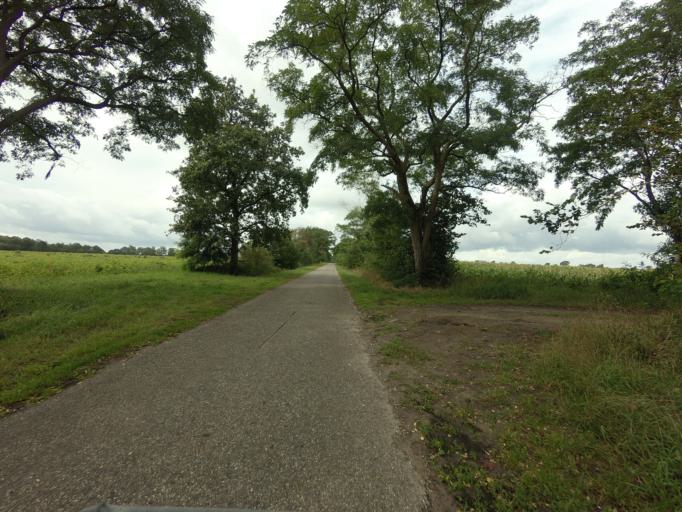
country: NL
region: Drenthe
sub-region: Gemeente Tynaarlo
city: Vries
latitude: 53.0982
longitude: 6.4962
